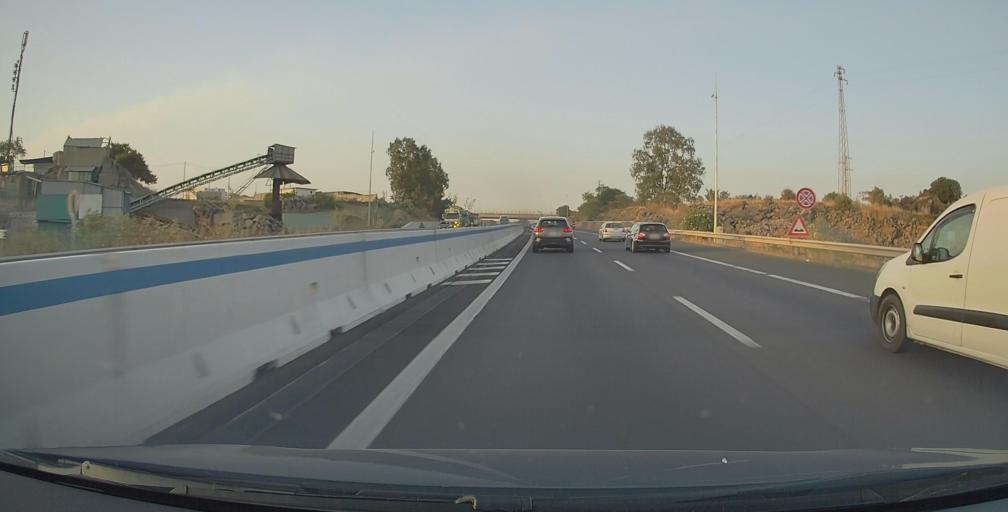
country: IT
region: Sicily
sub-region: Catania
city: Misterbianco
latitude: 37.5312
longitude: 15.0380
